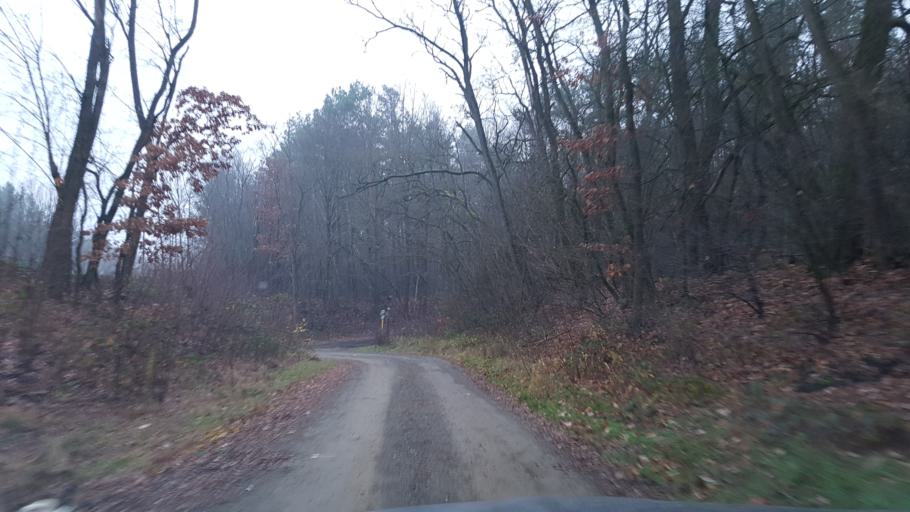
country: DE
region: Brandenburg
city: Ruckersdorf
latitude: 51.5430
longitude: 13.5759
